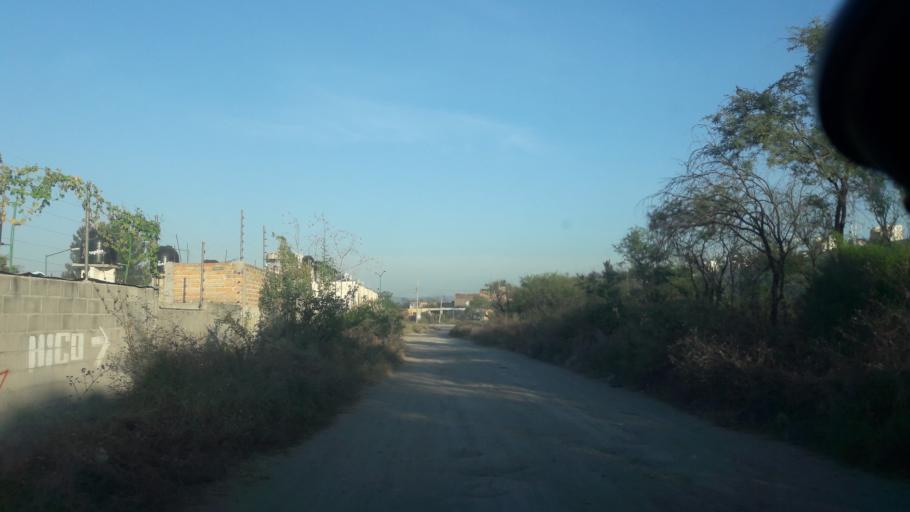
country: MX
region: Guanajuato
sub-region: Leon
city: Medina
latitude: 21.1651
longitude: -101.6347
